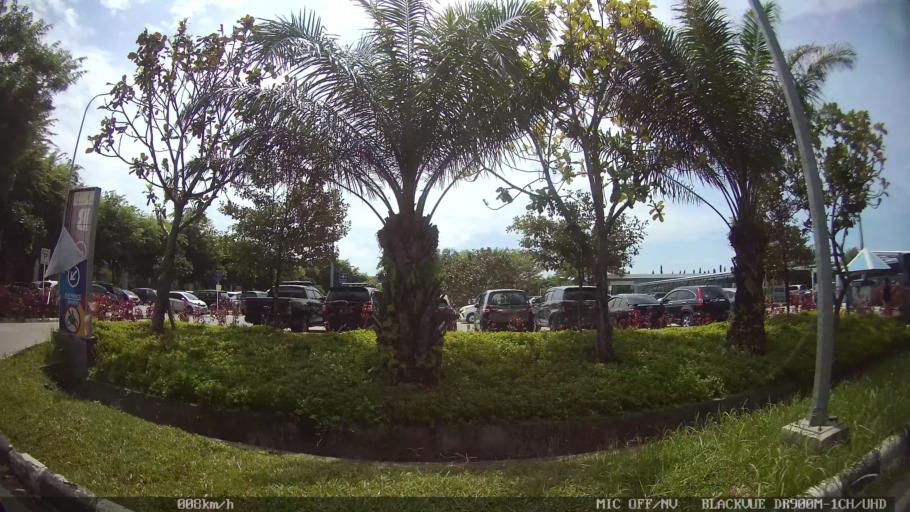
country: ID
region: North Sumatra
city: Percut
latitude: 3.6343
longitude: 98.8786
